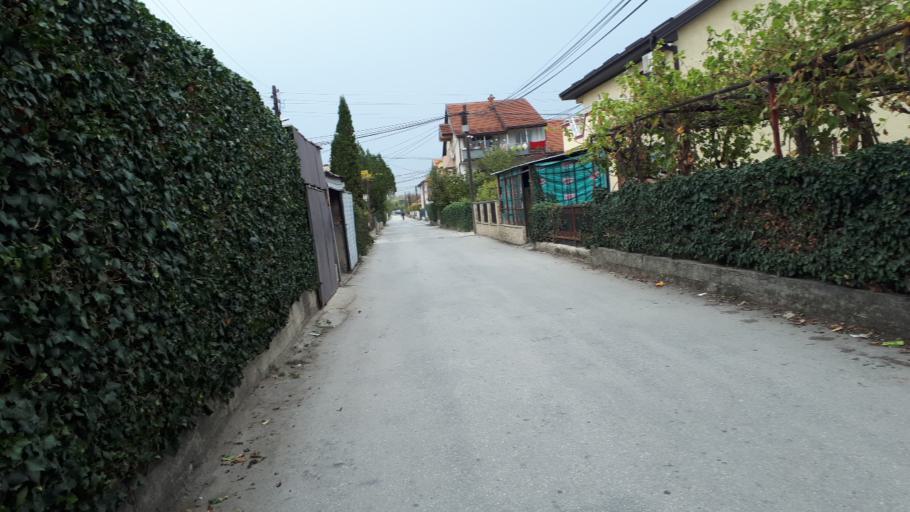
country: MK
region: Saraj
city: Saraj
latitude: 42.0192
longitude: 21.3556
